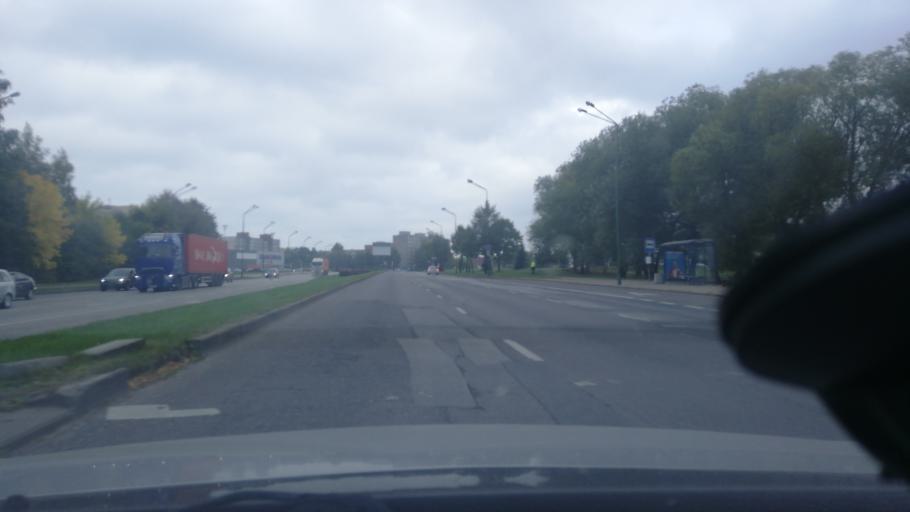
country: LT
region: Klaipedos apskritis
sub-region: Klaipeda
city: Klaipeda
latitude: 55.6753
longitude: 21.1935
